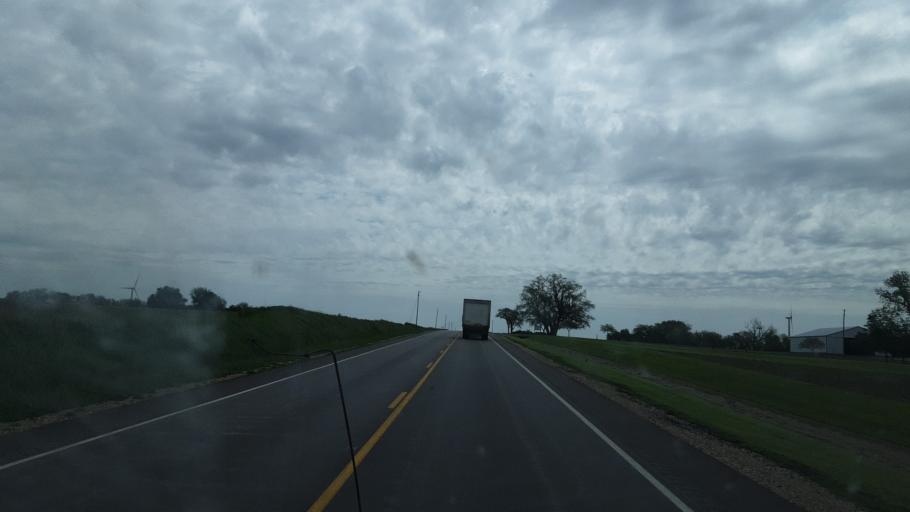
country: US
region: Illinois
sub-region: Tazewell County
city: Richmond
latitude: 40.3090
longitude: -89.4100
